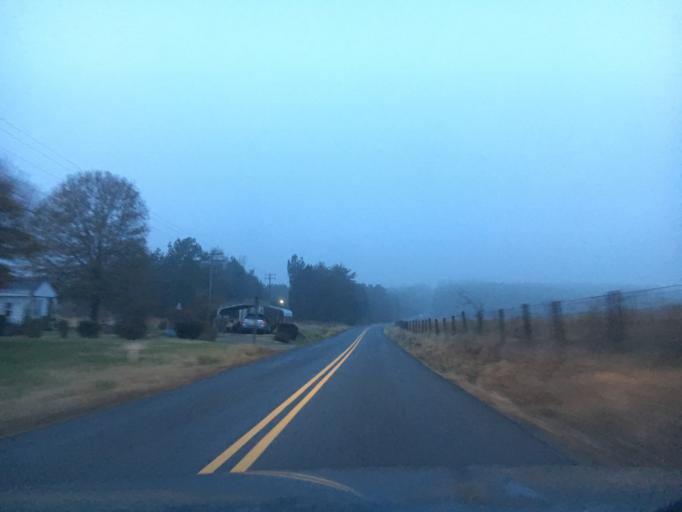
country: US
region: Virginia
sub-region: Halifax County
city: Mountain Road
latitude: 36.6811
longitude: -79.0294
